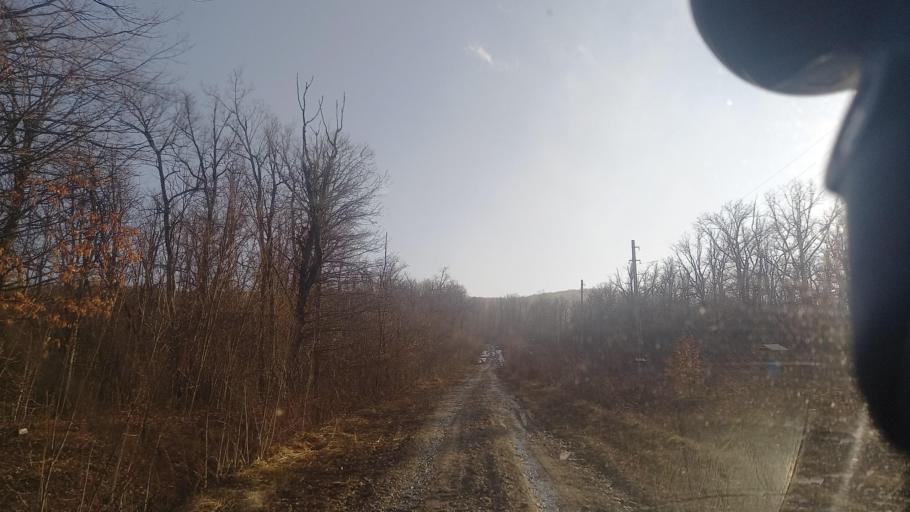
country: RU
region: Krasnodarskiy
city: Smolenskaya
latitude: 44.6730
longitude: 38.7965
